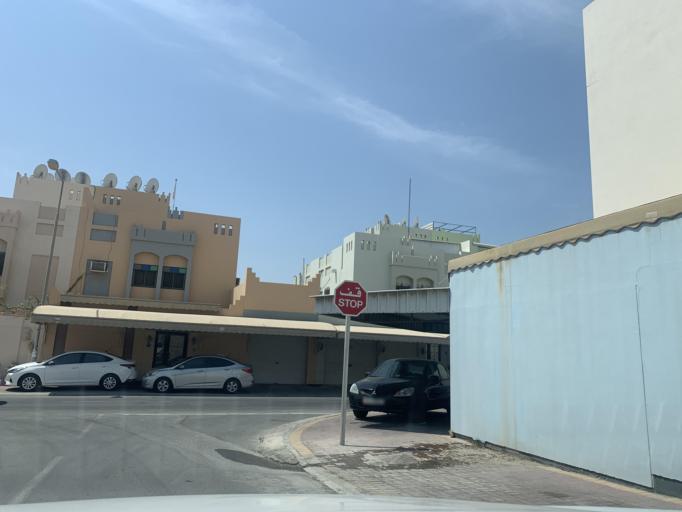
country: BH
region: Central Governorate
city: Madinat Hamad
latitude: 26.1399
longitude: 50.5002
